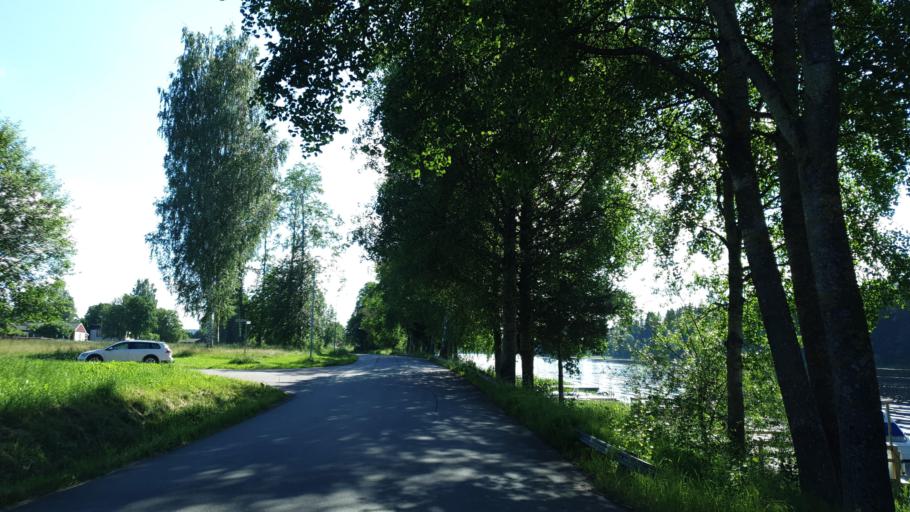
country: SE
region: Dalarna
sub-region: Avesta Kommun
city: Avesta
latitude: 60.1272
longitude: 16.2544
